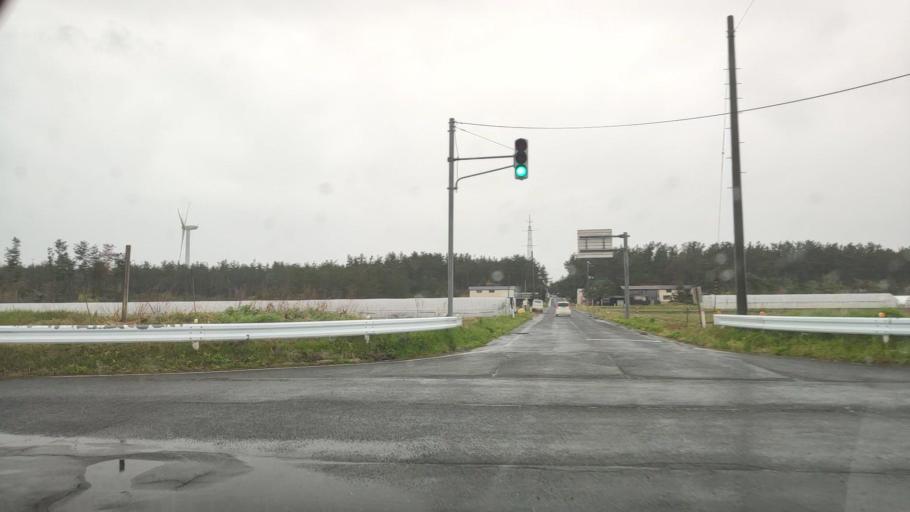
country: JP
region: Akita
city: Noshiromachi
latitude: 40.0978
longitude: 139.9671
